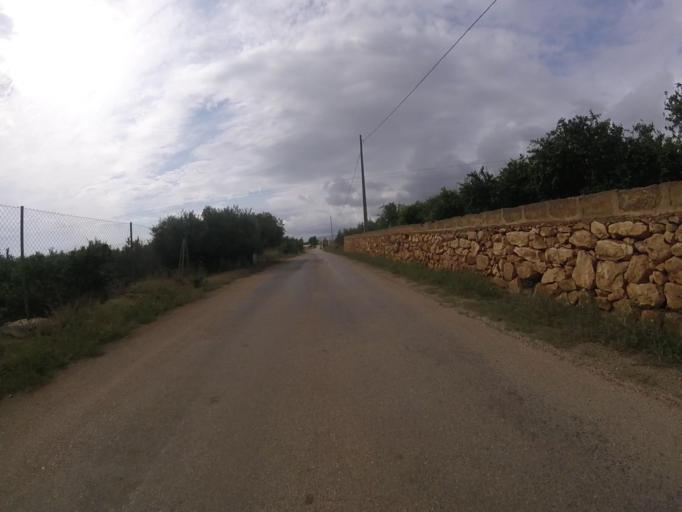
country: ES
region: Valencia
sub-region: Provincia de Castello
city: Torreblanca
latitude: 40.2037
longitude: 0.1817
